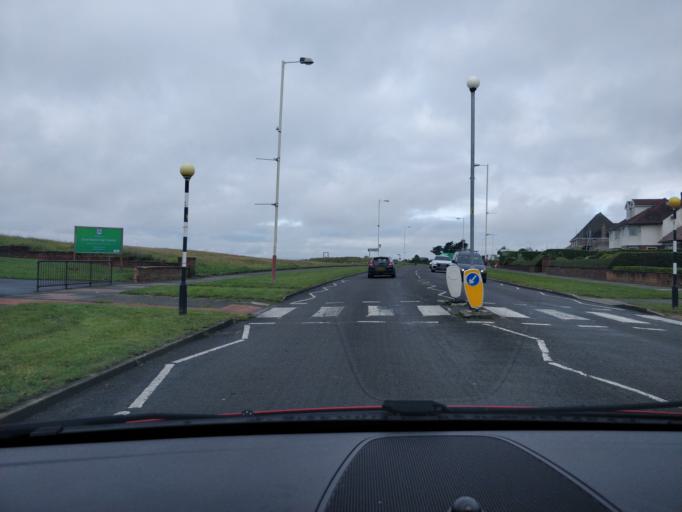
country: GB
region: England
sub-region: Sefton
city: Southport
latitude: 53.6241
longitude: -3.0273
